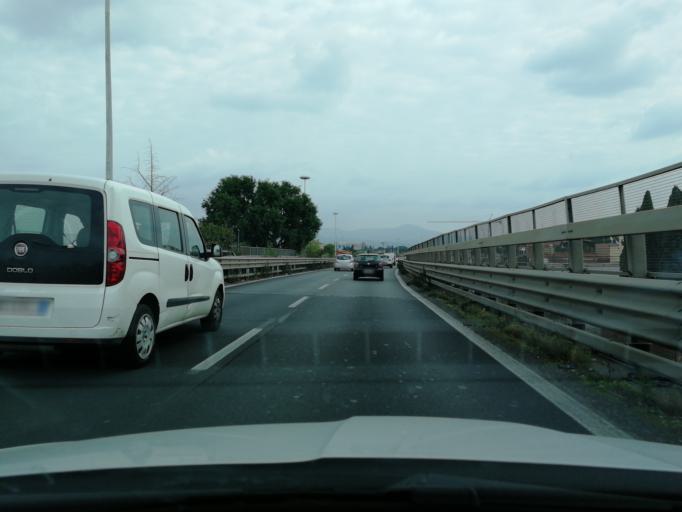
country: IT
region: Latium
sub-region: Citta metropolitana di Roma Capitale
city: Ciampino
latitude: 41.8429
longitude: 12.5839
